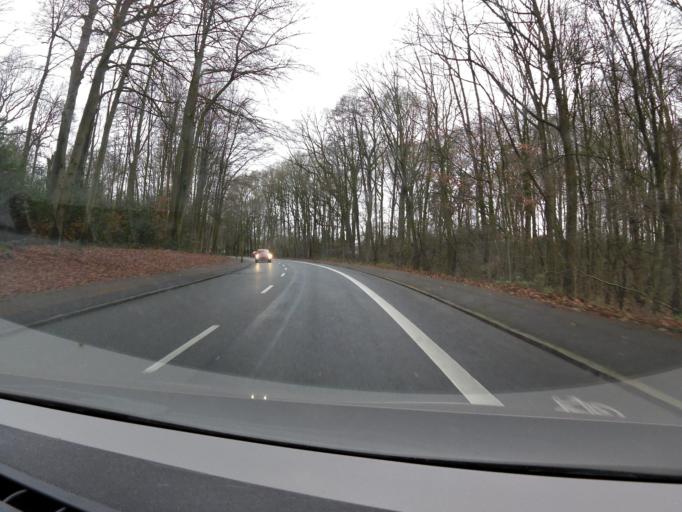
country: DE
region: North Rhine-Westphalia
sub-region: Regierungsbezirk Arnsberg
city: Dortmund
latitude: 51.4567
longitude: 7.4709
